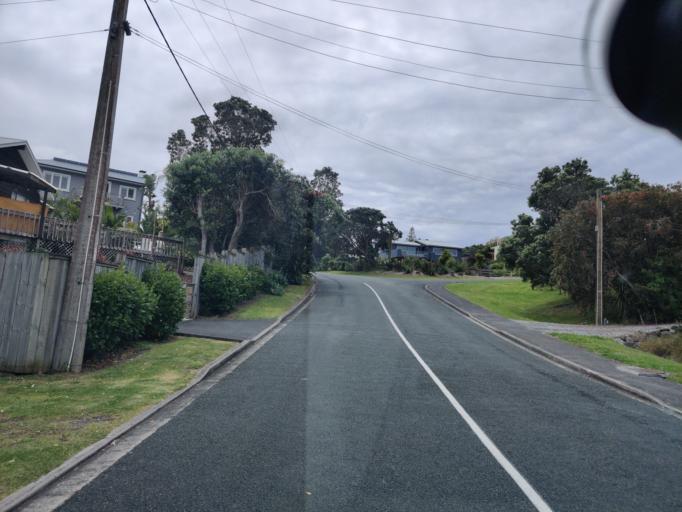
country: NZ
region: Auckland
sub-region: Auckland
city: Warkworth
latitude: -36.2985
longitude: 174.7984
